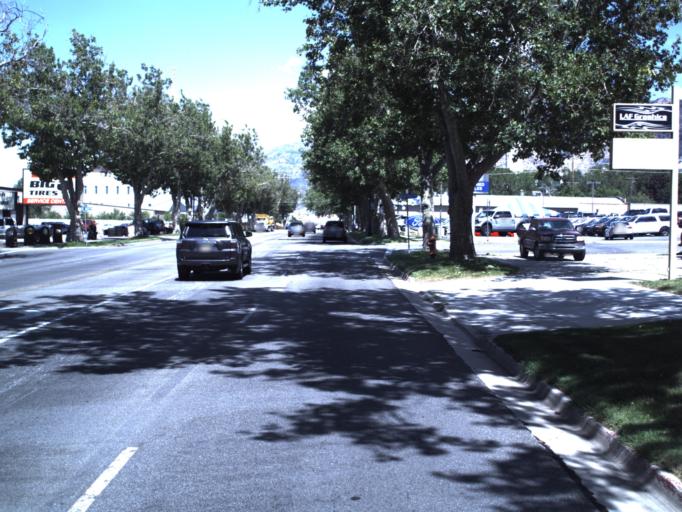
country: US
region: Utah
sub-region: Box Elder County
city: Brigham City
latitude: 41.5027
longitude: -112.0158
